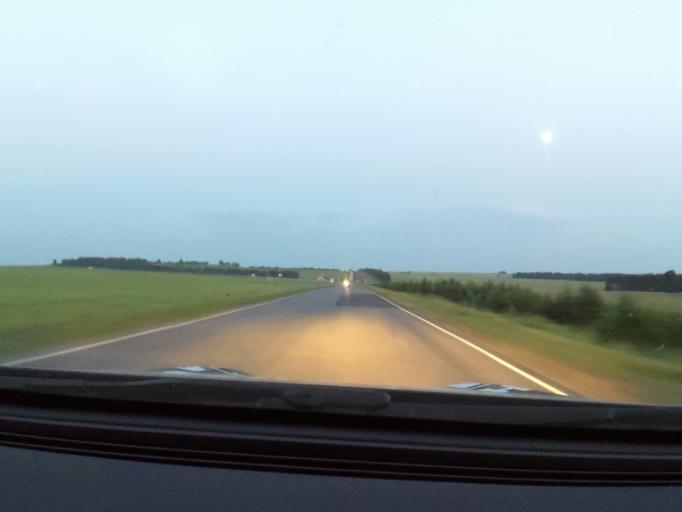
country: RU
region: Bashkortostan
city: Duvan
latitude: 56.0832
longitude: 58.0829
